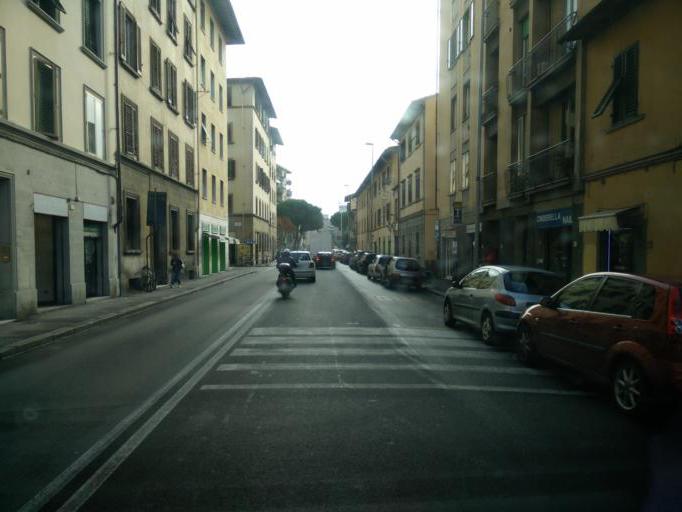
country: IT
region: Tuscany
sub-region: Province of Florence
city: Florence
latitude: 43.7911
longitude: 11.2200
